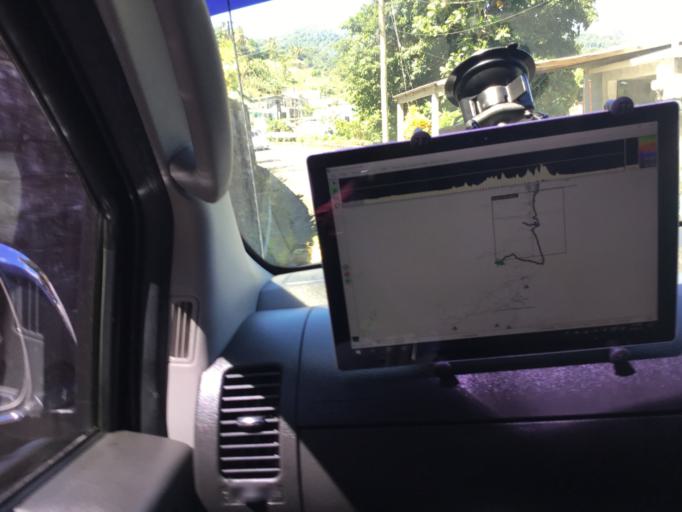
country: VC
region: Charlotte
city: Byera Village
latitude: 13.2440
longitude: -61.1397
